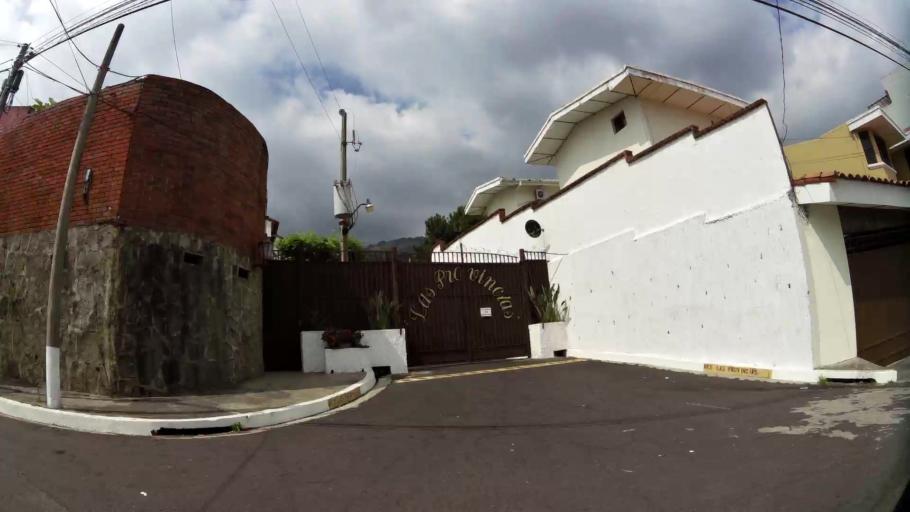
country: SV
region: La Libertad
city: Santa Tecla
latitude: 13.7129
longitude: -89.2513
